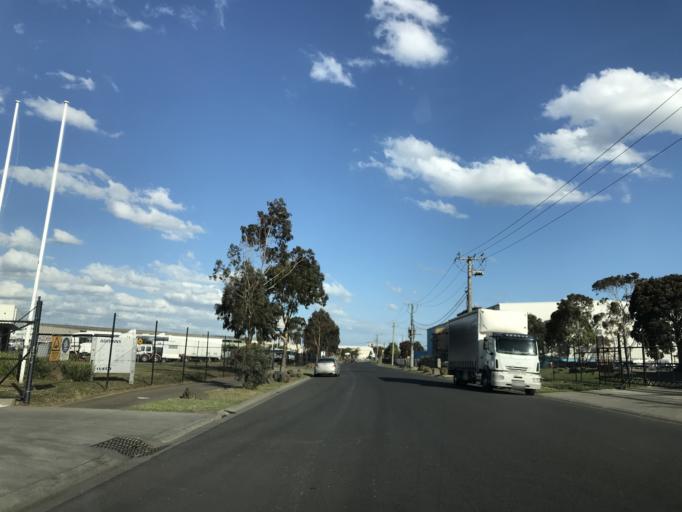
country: AU
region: Victoria
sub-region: Brimbank
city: Sunshine West
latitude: -37.8156
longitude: 144.8045
